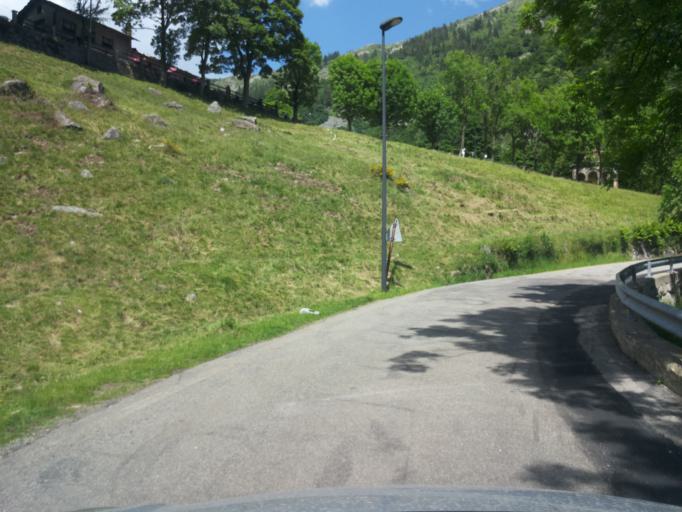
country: IT
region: Piedmont
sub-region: Provincia di Biella
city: Campiglia Cervo
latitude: 45.6307
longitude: 7.9779
